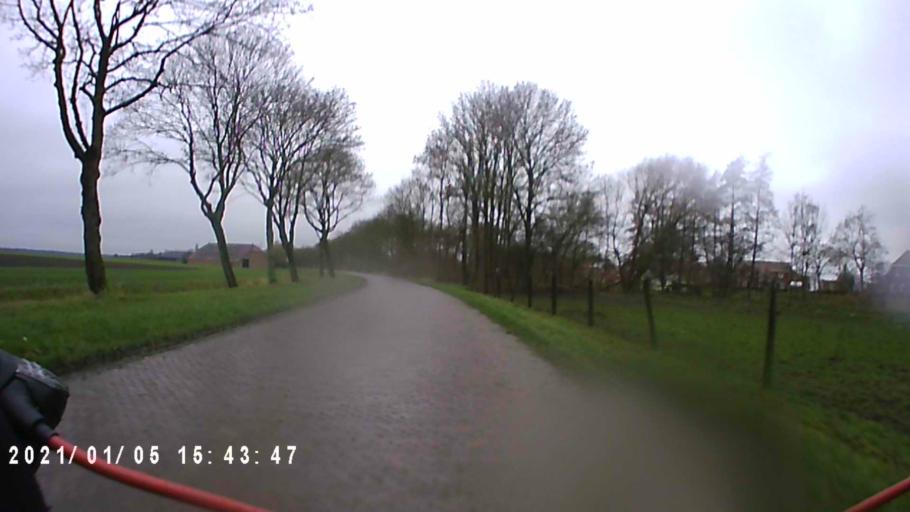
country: NL
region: Groningen
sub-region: Gemeente  Oldambt
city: Winschoten
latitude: 53.2081
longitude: 7.1241
